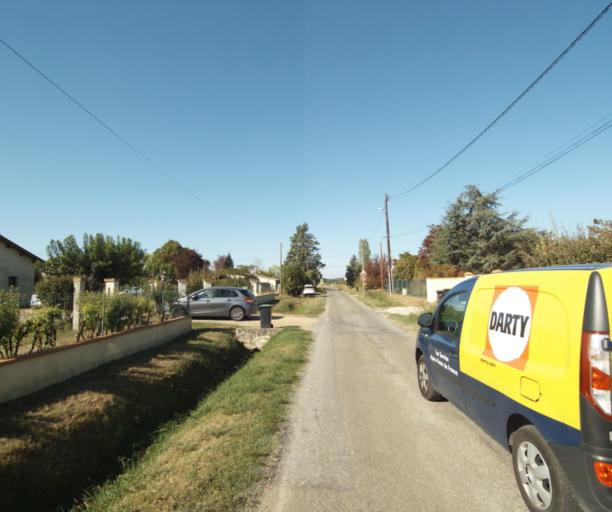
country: FR
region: Midi-Pyrenees
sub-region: Departement du Tarn-et-Garonne
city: Verdun-sur-Garonne
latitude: 43.8453
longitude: 1.2186
